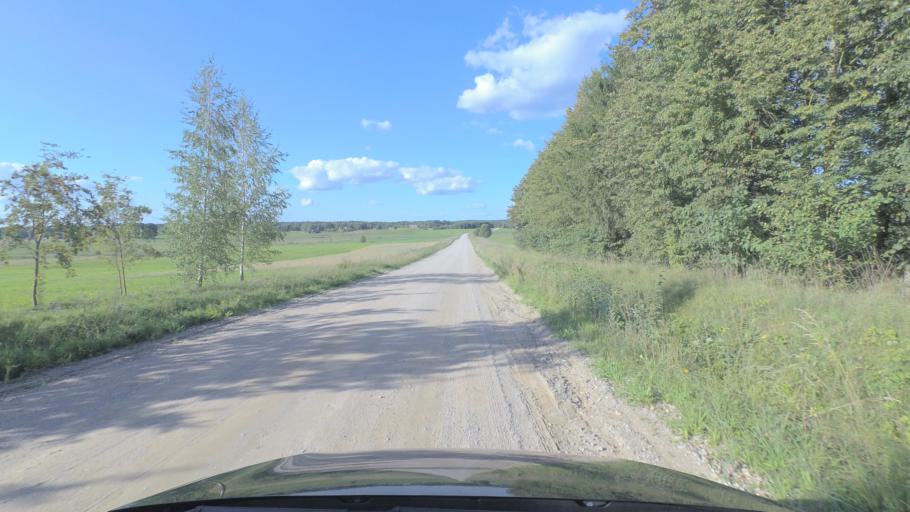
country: LT
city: Pabrade
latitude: 55.1302
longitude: 25.7057
